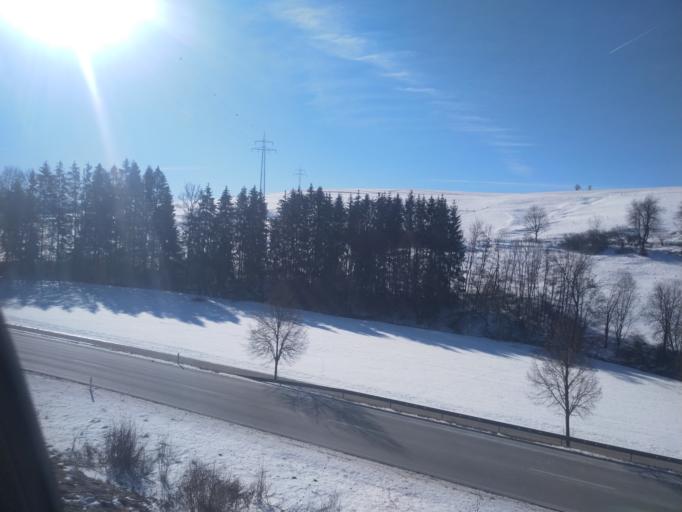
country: DE
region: Baden-Wuerttemberg
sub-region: Freiburg Region
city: Aldingen
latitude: 48.1168
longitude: 8.6875
